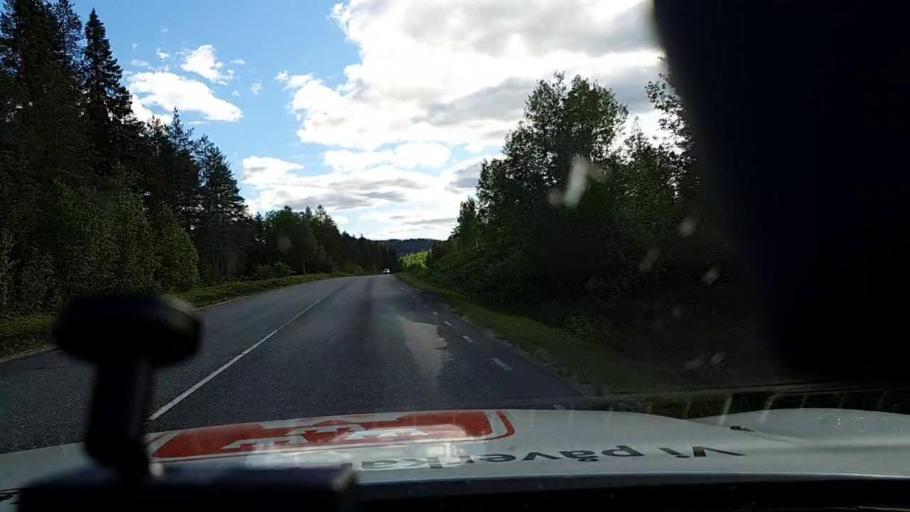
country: FI
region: Lapland
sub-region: Torniolaakso
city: Ylitornio
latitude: 66.3329
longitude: 23.6385
